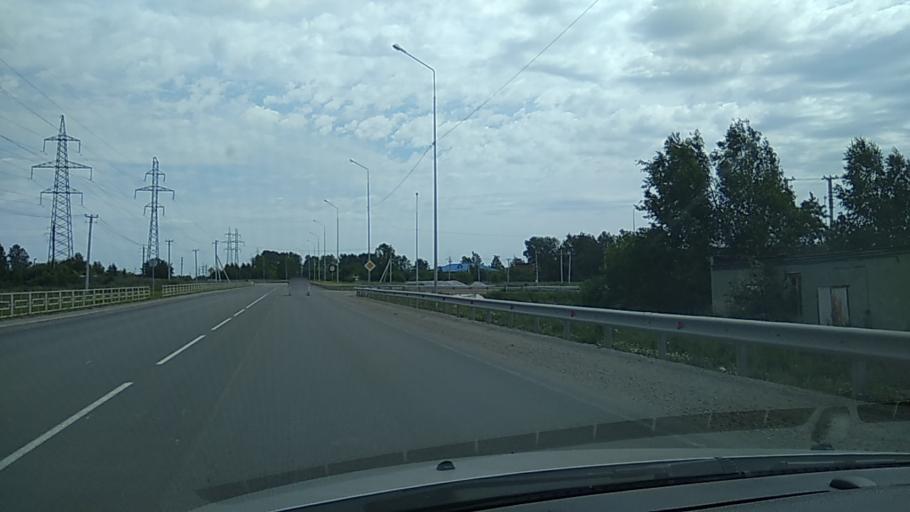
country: RU
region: Sverdlovsk
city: Verkhnyaya Pyshma
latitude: 56.9475
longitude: 60.5998
